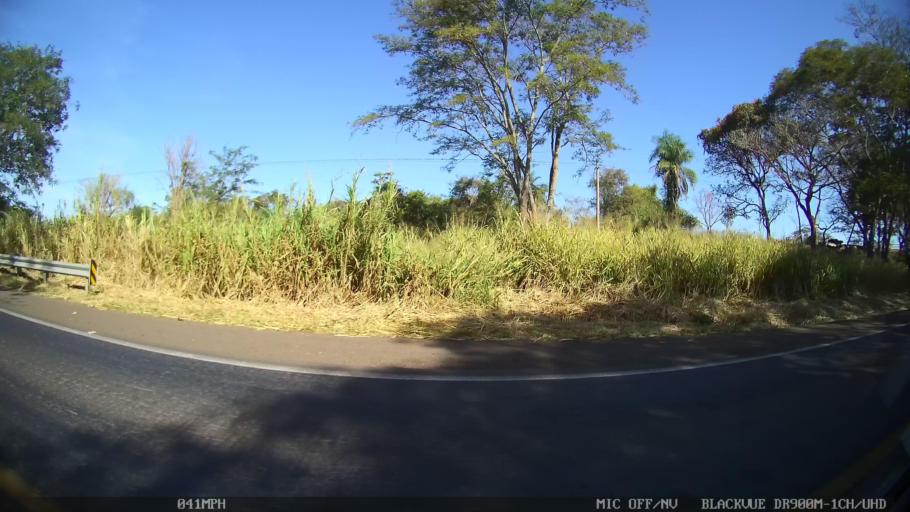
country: BR
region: Sao Paulo
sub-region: Olimpia
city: Olimpia
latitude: -20.6306
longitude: -48.8030
